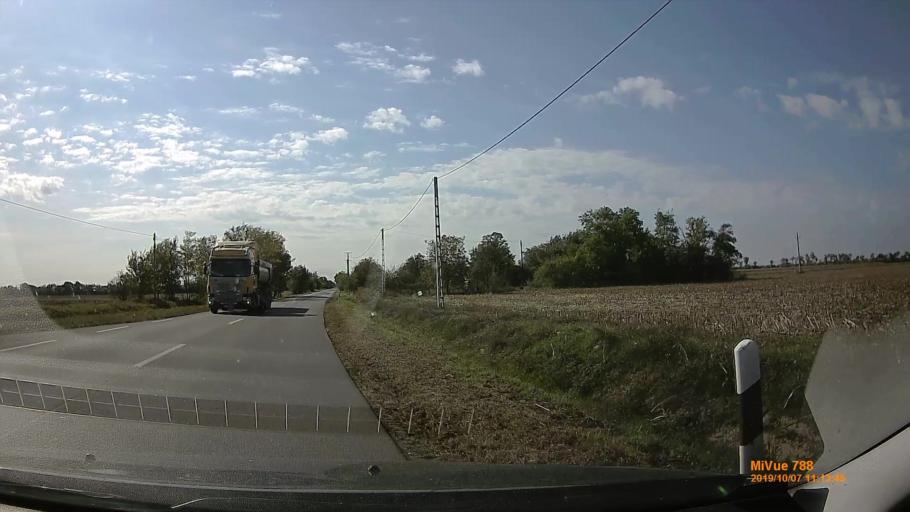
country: HU
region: Bekes
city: Kondoros
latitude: 46.7336
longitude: 20.7820
